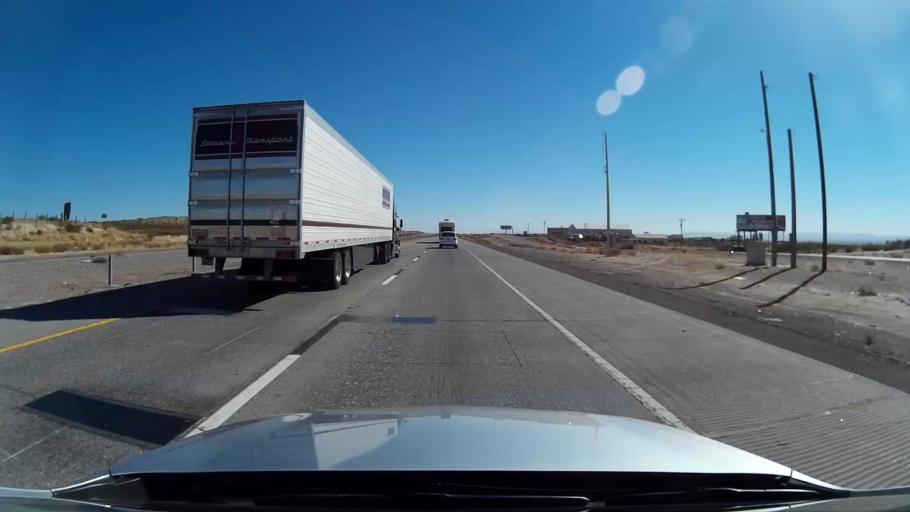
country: US
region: Texas
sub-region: El Paso County
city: Sparks
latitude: 31.6344
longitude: -106.2204
